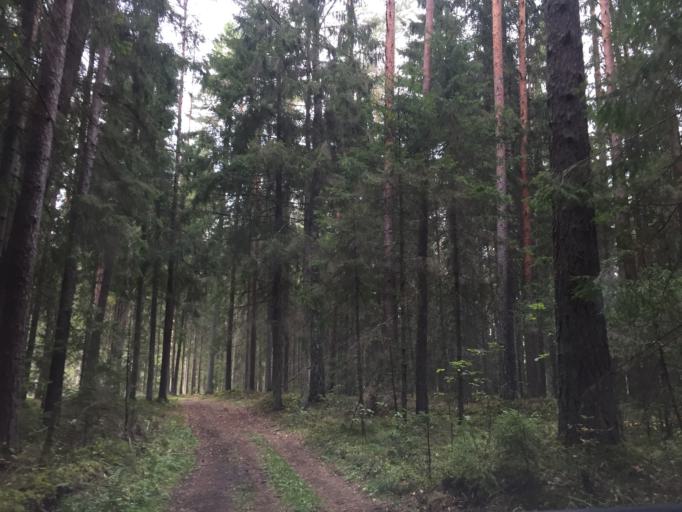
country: LV
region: Baldone
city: Baldone
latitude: 56.7822
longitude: 24.4439
